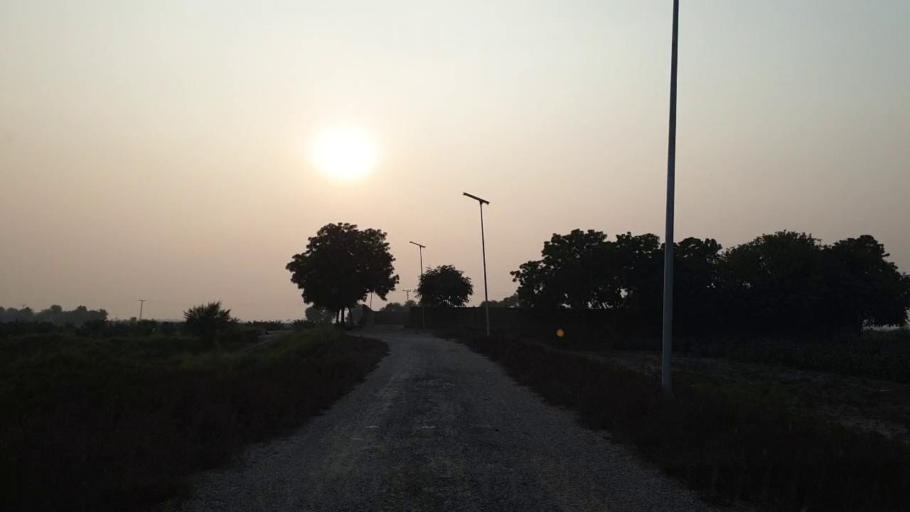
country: PK
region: Sindh
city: Bhan
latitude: 26.5055
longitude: 67.7129
